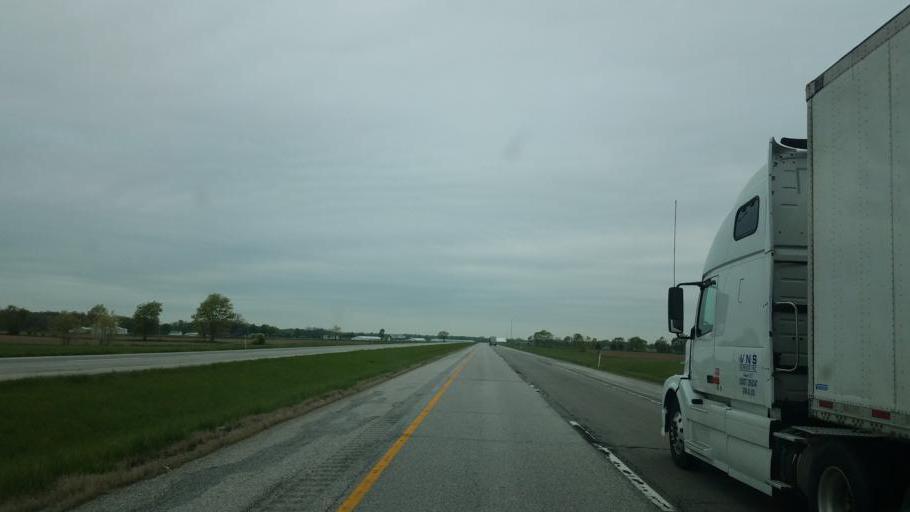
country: US
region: Michigan
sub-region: Saint Joseph County
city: Sturgis
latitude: 41.7457
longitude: -85.5185
